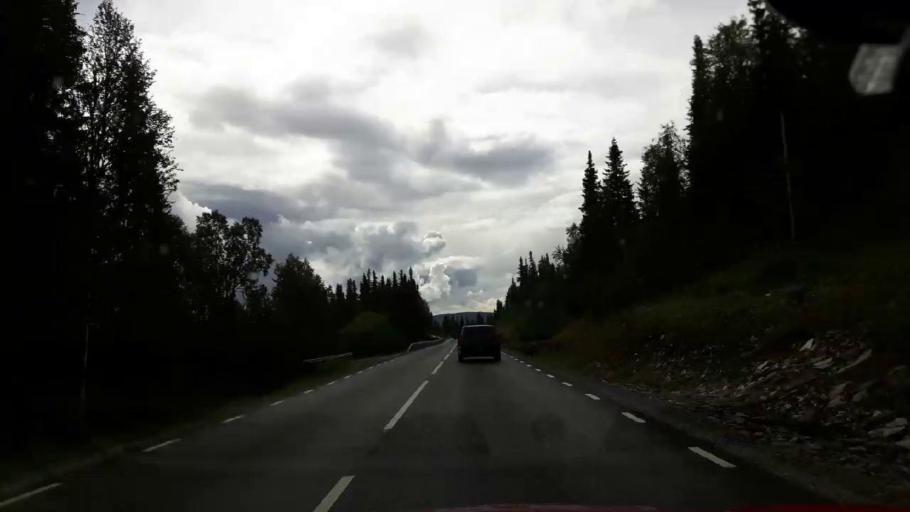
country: NO
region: Nord-Trondelag
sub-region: Royrvik
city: Royrvik
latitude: 64.8351
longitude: 14.1270
